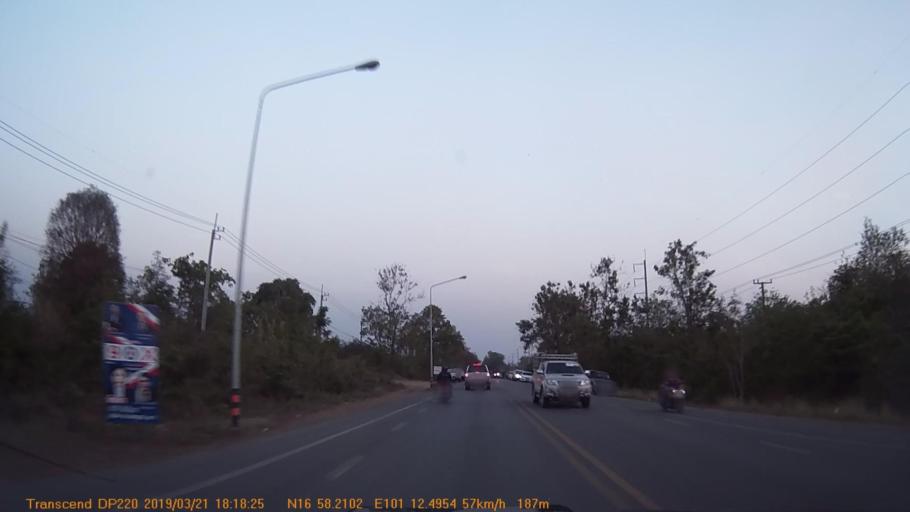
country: TH
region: Phetchabun
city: Lom Kao
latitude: 16.9699
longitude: 101.2084
